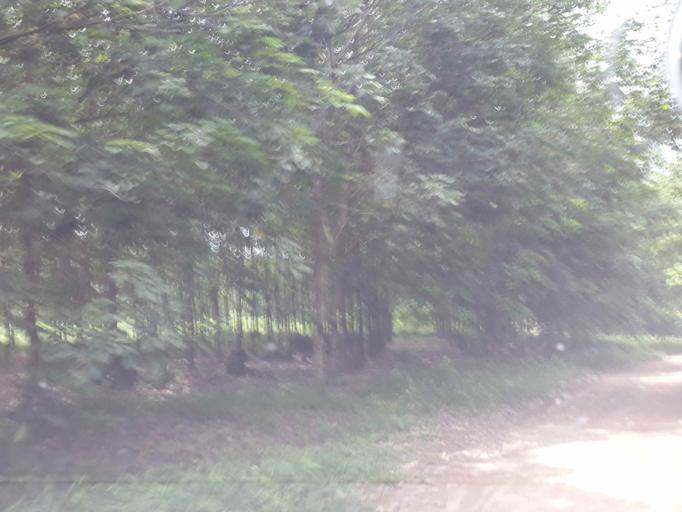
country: ID
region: Lampung
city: Natar
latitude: -5.2618
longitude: 105.2917
